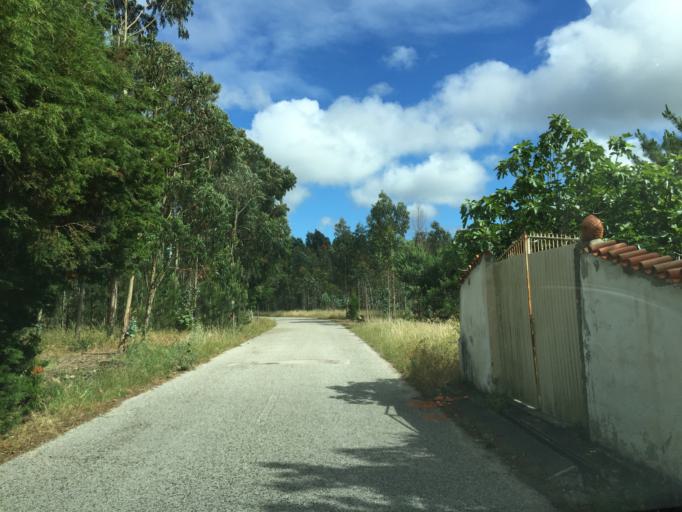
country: PT
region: Coimbra
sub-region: Figueira da Foz
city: Tavarede
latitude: 40.2120
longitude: -8.8418
